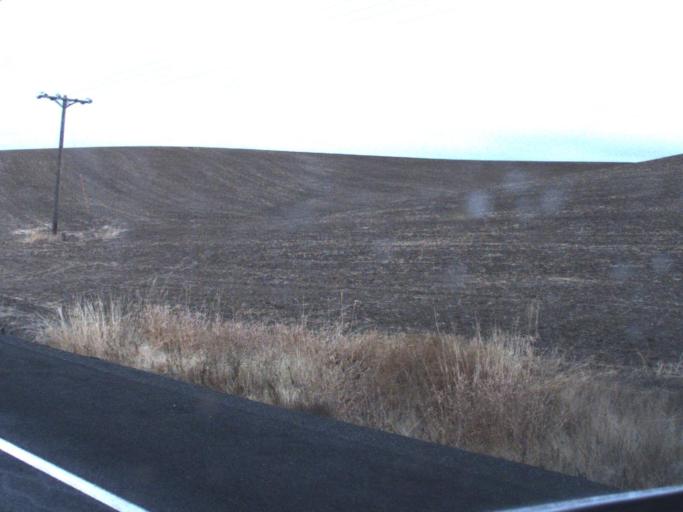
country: US
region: Washington
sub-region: Whitman County
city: Pullman
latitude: 46.6616
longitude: -117.1930
